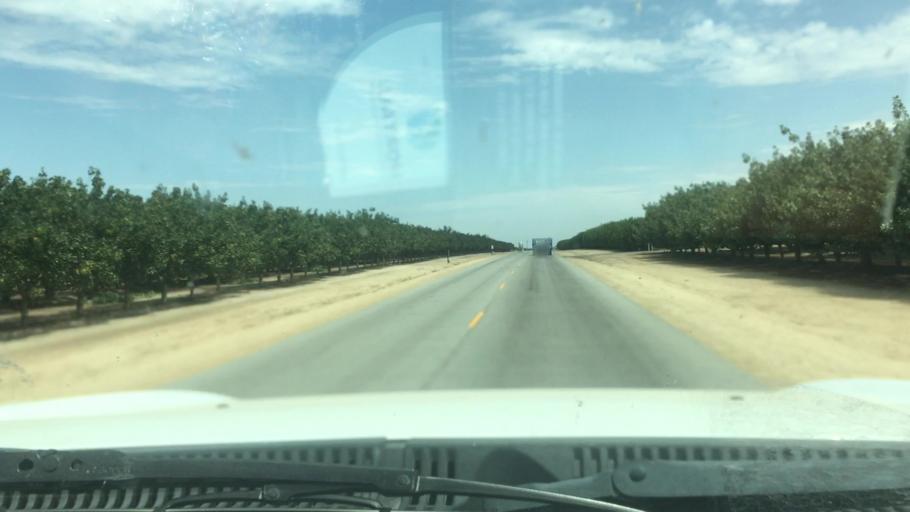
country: US
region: California
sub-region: Kern County
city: McFarland
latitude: 35.5834
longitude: -119.1511
